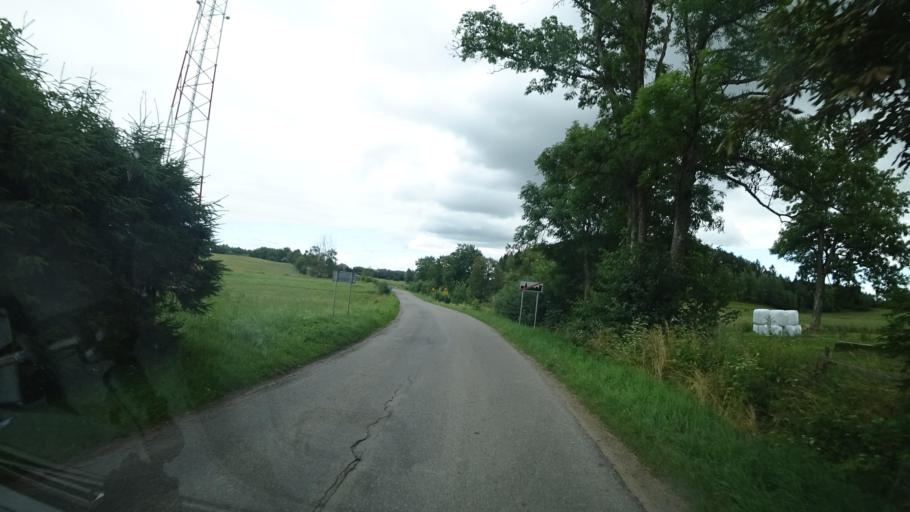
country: PL
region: Podlasie
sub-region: Powiat suwalski
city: Filipow
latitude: 54.2838
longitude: 22.5209
